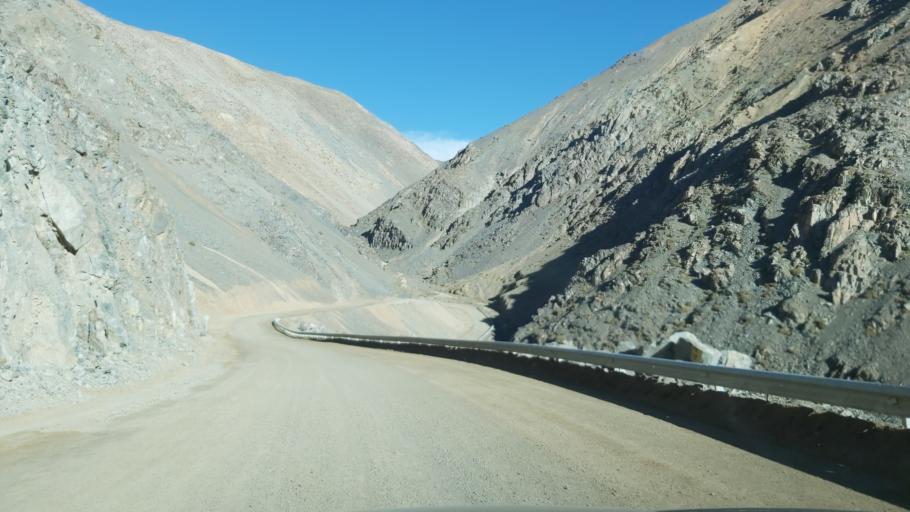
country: CL
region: Atacama
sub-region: Provincia de Chanaral
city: Diego de Almagro
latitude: -26.4802
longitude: -69.3185
